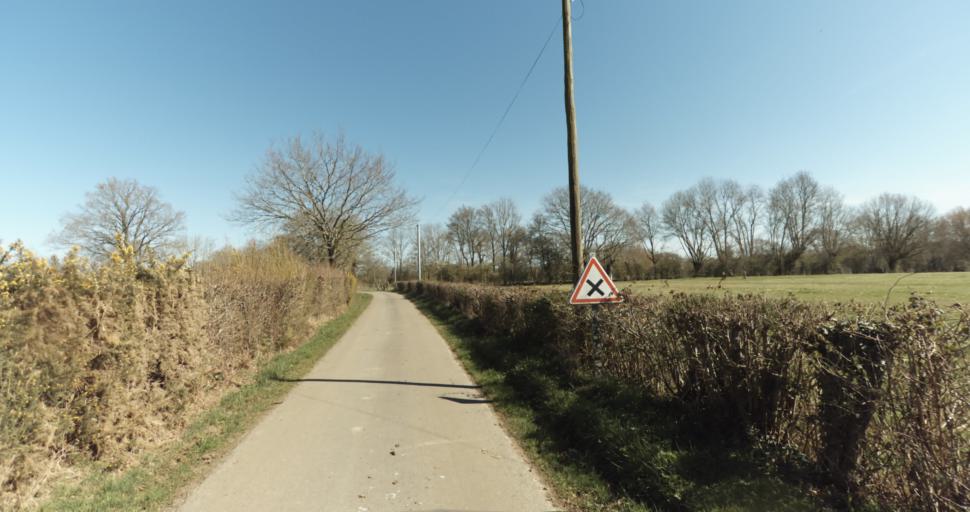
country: FR
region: Lower Normandy
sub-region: Departement du Calvados
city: Livarot
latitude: 48.9933
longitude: 0.0860
